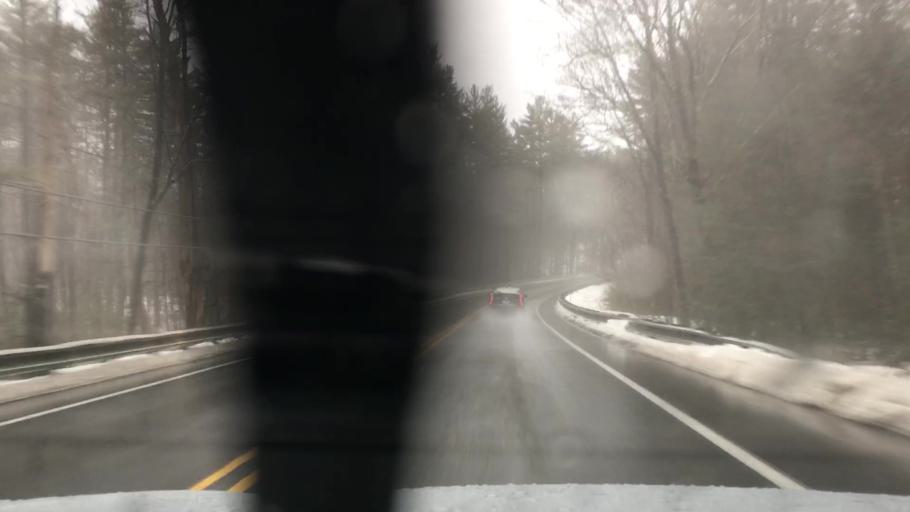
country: US
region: Massachusetts
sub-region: Franklin County
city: Orange
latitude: 42.5332
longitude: -72.3189
